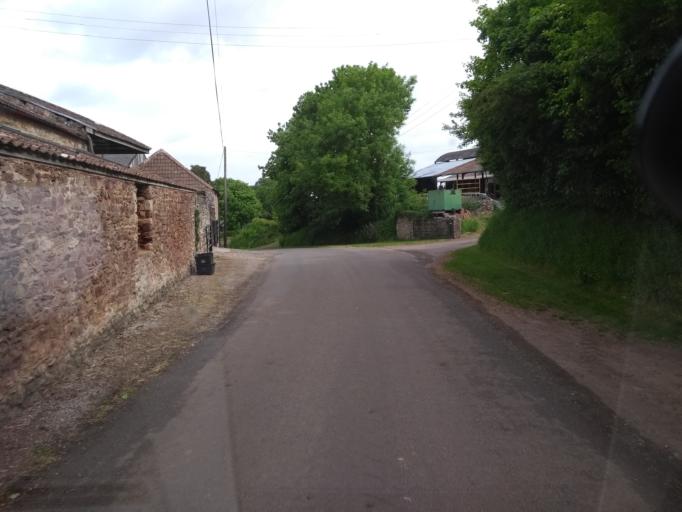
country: GB
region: England
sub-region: Somerset
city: North Petherton
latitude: 51.1276
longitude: -3.1076
